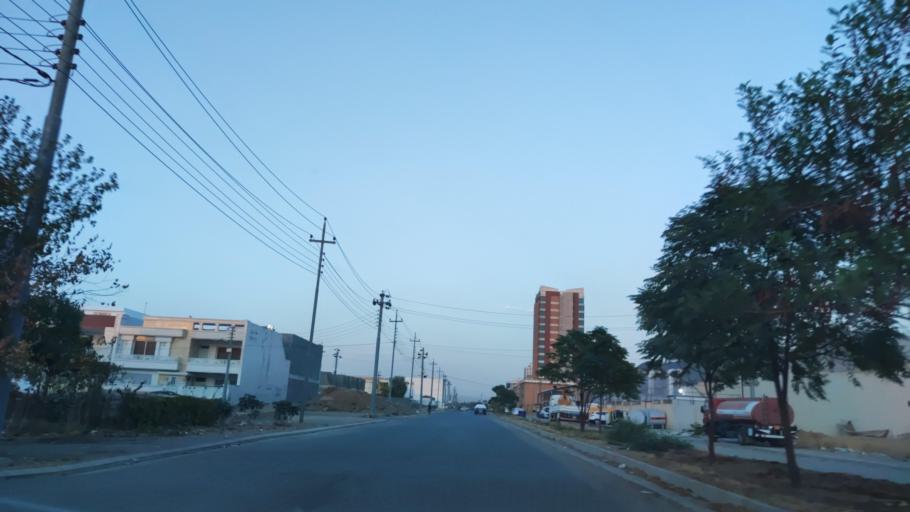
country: IQ
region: Arbil
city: Erbil
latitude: 36.1798
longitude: 43.9570
